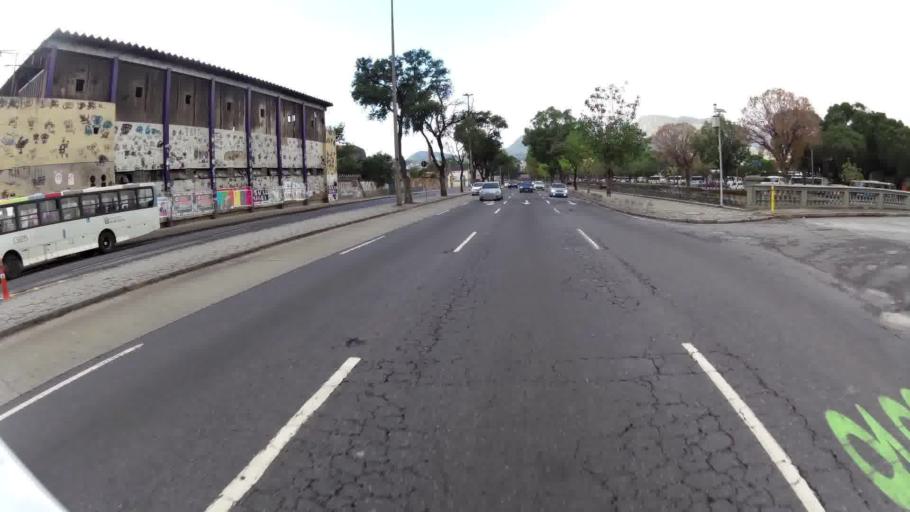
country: BR
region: Rio de Janeiro
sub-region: Rio De Janeiro
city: Rio de Janeiro
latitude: -22.9031
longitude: -43.2098
